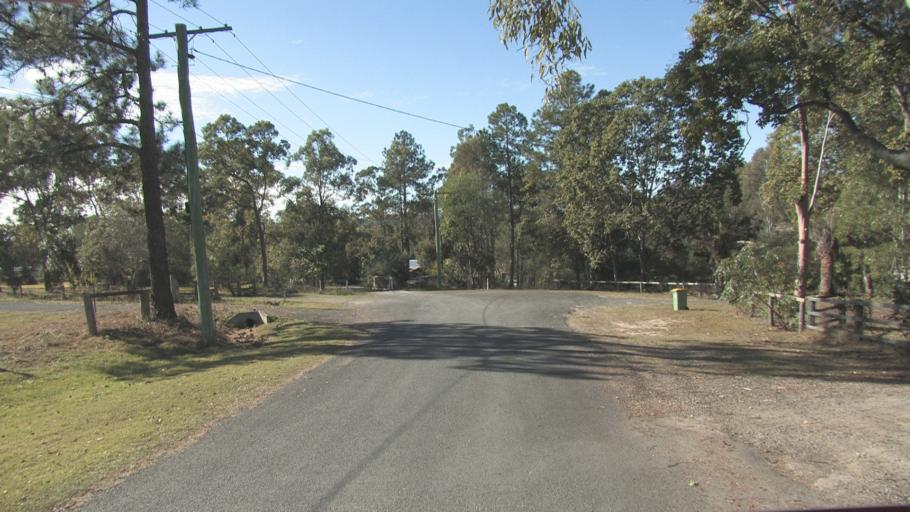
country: AU
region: Queensland
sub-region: Logan
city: Chambers Flat
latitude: -27.7794
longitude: 153.0895
